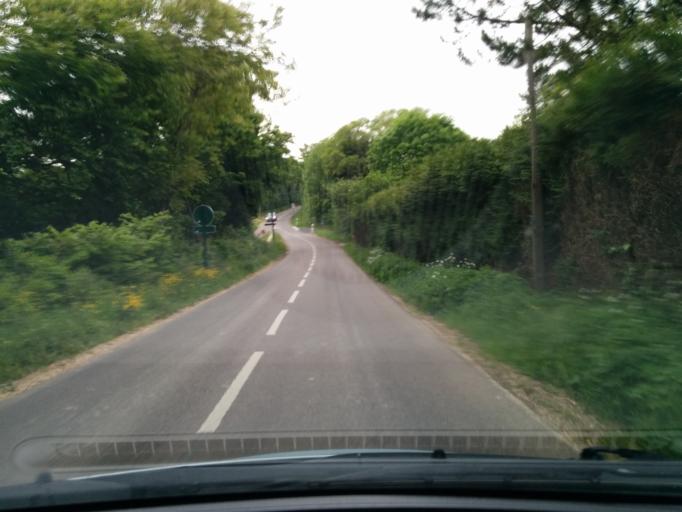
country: FR
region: Haute-Normandie
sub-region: Departement de l'Eure
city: Gasny
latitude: 49.0857
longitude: 1.6330
